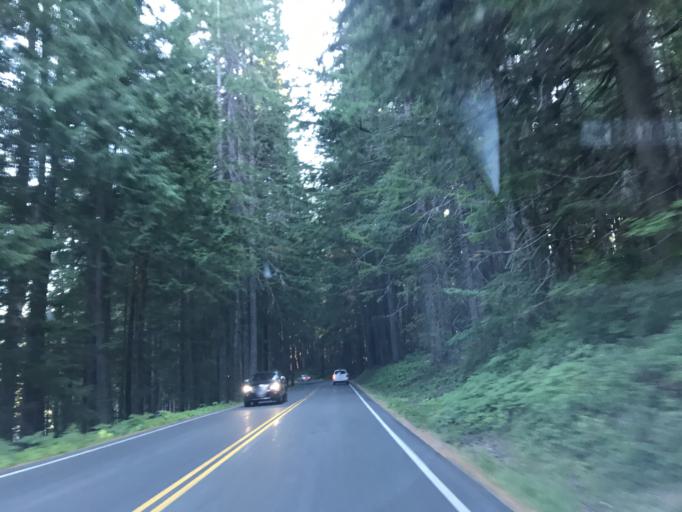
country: US
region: Washington
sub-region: Pierce County
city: Eatonville
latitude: 46.7332
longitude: -121.8316
